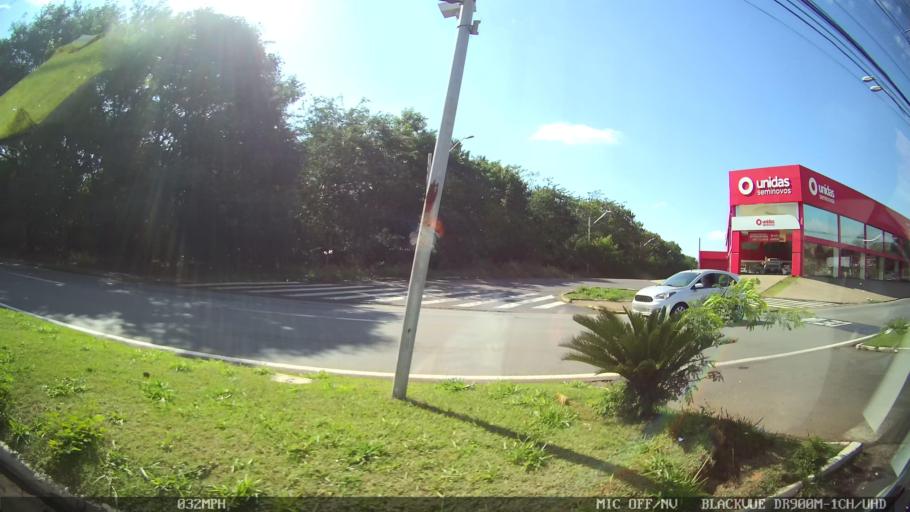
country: BR
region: Sao Paulo
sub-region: Americana
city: Americana
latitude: -22.7459
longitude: -47.3065
